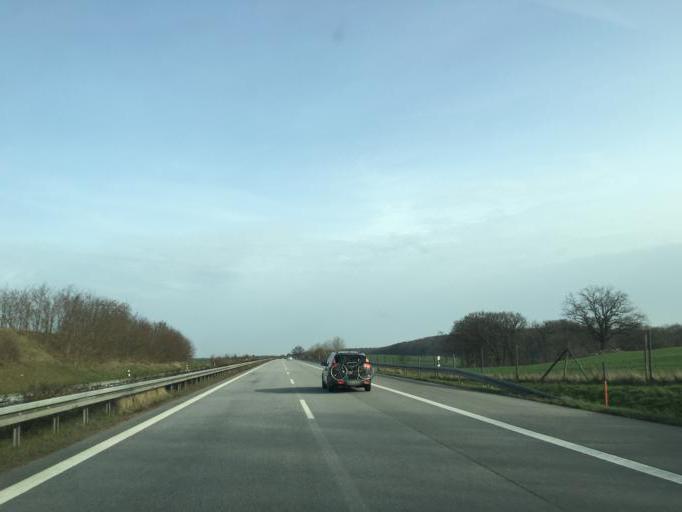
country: DE
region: Mecklenburg-Vorpommern
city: Malchow
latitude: 53.3946
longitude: 12.4479
